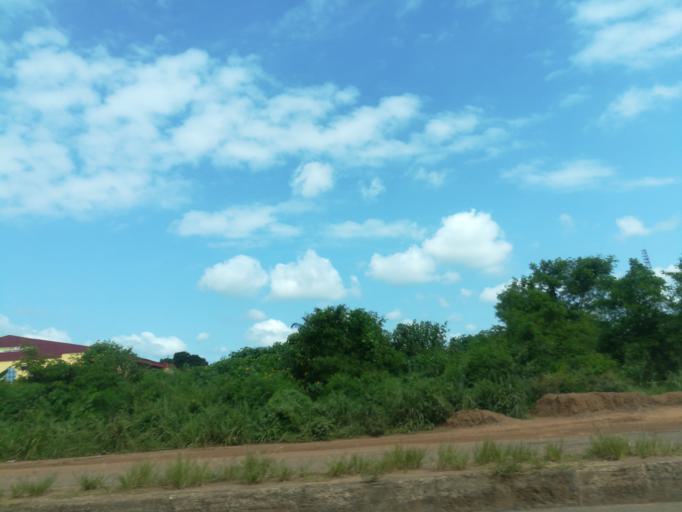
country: NG
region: Oyo
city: Egbeda
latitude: 7.4240
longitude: 3.9850
